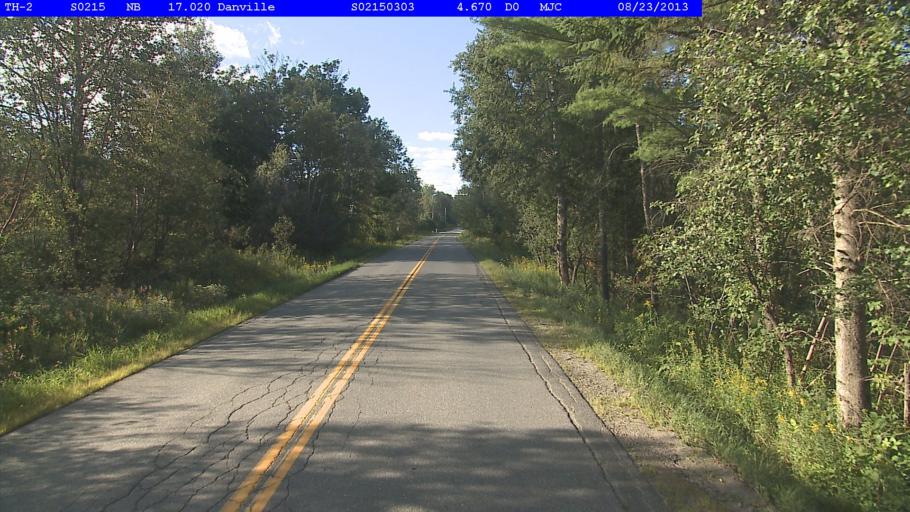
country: US
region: Vermont
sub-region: Caledonia County
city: St Johnsbury
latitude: 44.4312
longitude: -72.1409
